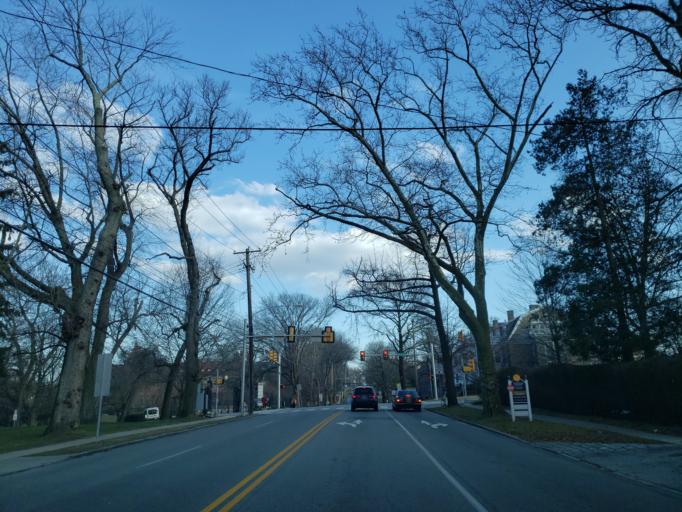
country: US
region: Pennsylvania
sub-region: Montgomery County
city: Bryn Mawr
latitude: 40.0233
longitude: -75.3157
